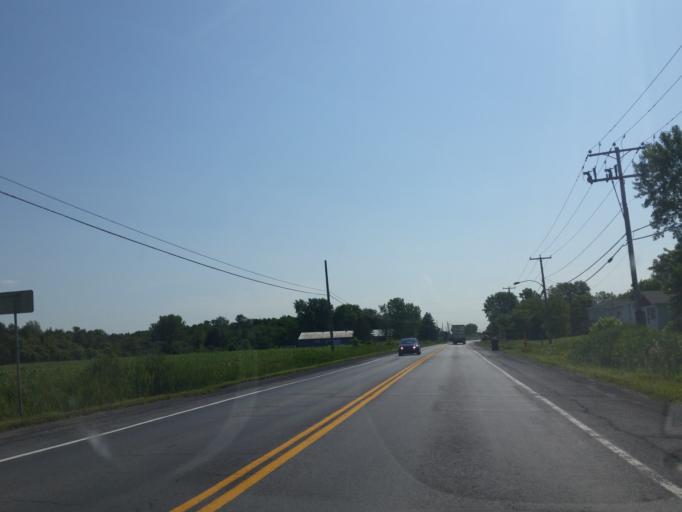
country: CA
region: Quebec
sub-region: Monteregie
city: Saint-Jean-sur-Richelieu
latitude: 45.3033
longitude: -73.3175
